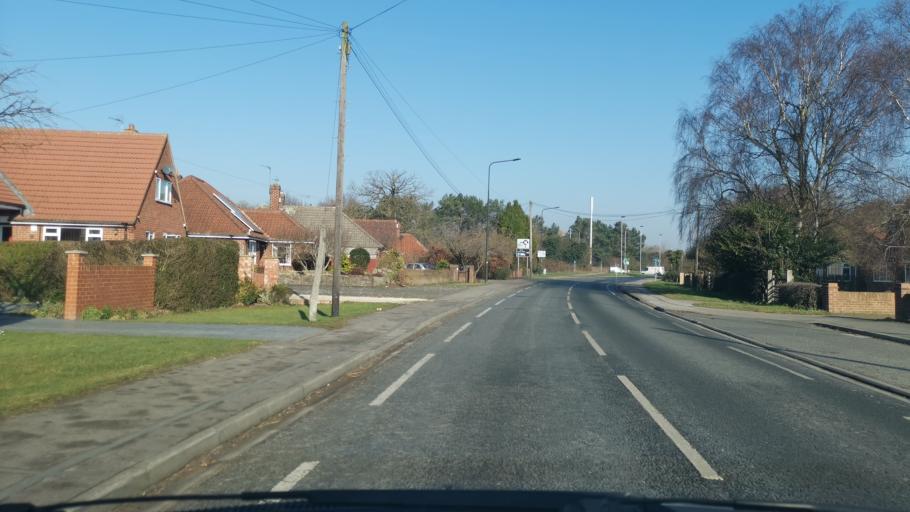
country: GB
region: England
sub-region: City of York
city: Huntington
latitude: 54.0035
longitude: -1.0571
